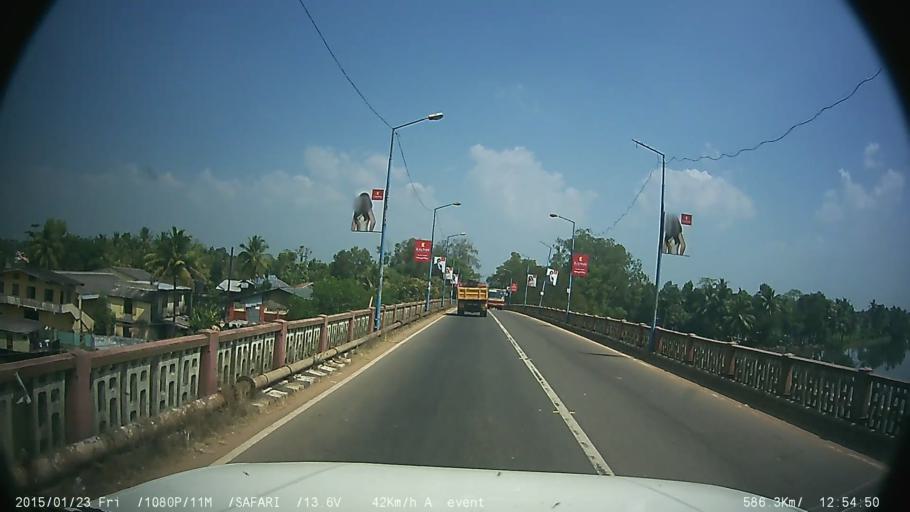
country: IN
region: Kerala
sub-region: Kottayam
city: Changanacheri
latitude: 9.4195
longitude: 76.4922
